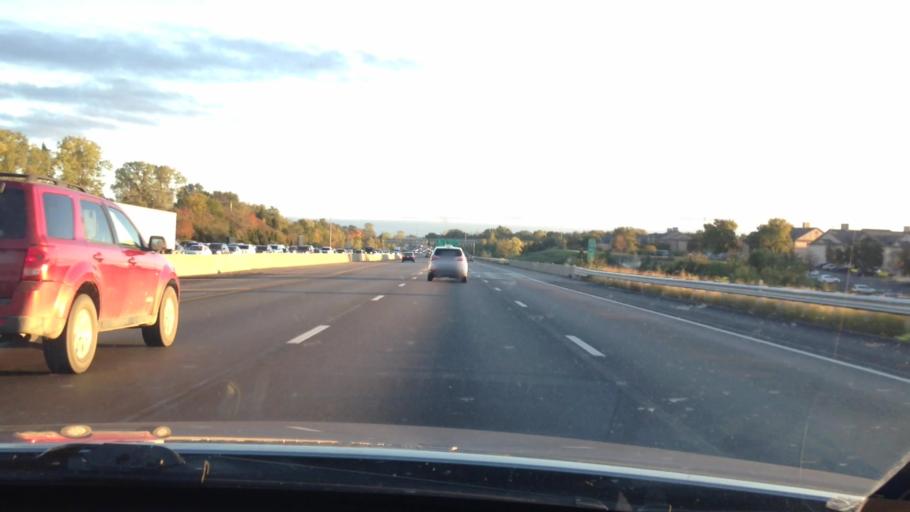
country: US
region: Missouri
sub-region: Jackson County
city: Raytown
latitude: 39.0321
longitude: -94.5006
